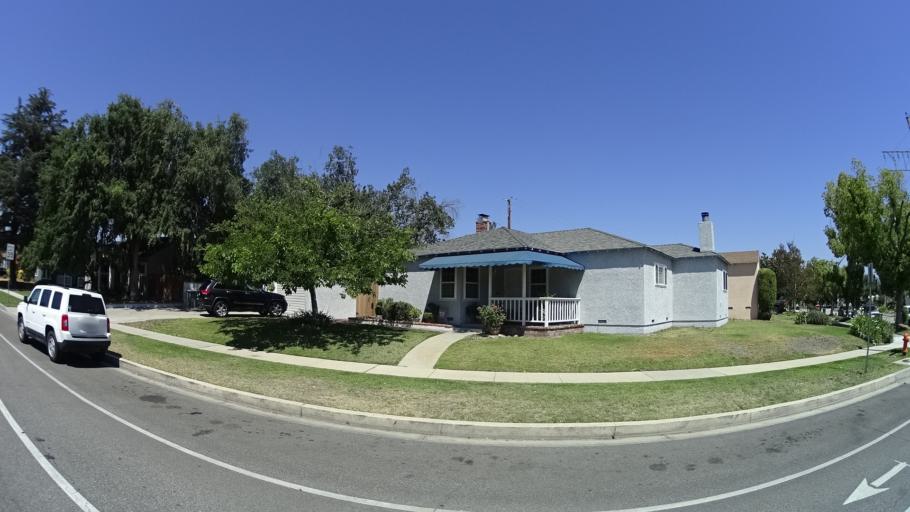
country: US
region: California
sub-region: Los Angeles County
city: North Hollywood
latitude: 34.1802
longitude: -118.3589
